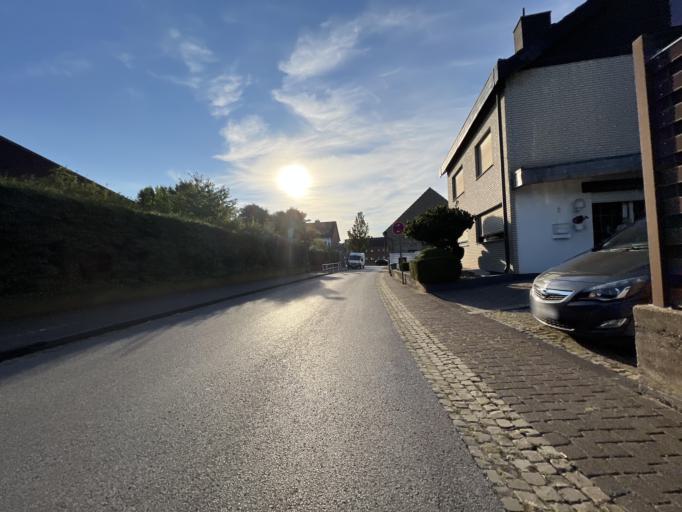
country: DE
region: North Rhine-Westphalia
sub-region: Regierungsbezirk Koln
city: Dueren
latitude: 50.7907
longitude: 6.4430
